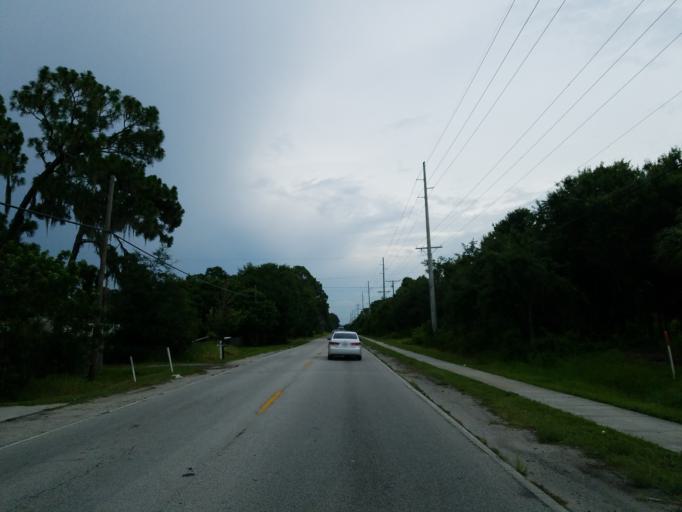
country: US
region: Florida
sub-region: Hillsborough County
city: Gibsonton
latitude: 27.8351
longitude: -82.3602
